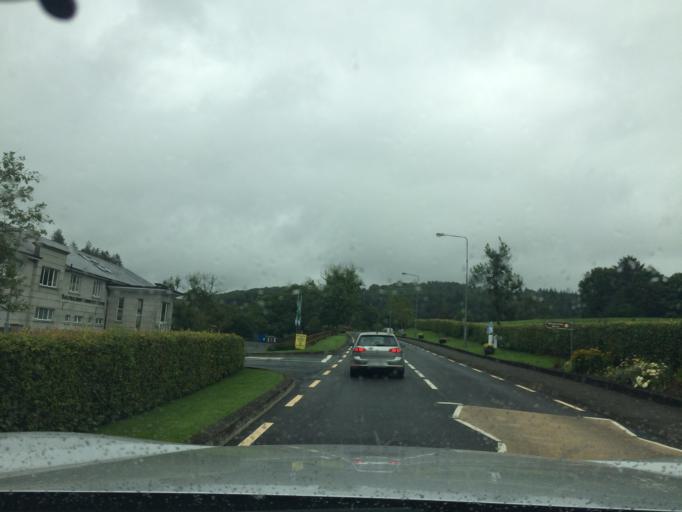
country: IE
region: Munster
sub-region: South Tipperary
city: Cluain Meala
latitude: 52.2670
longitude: -7.7160
